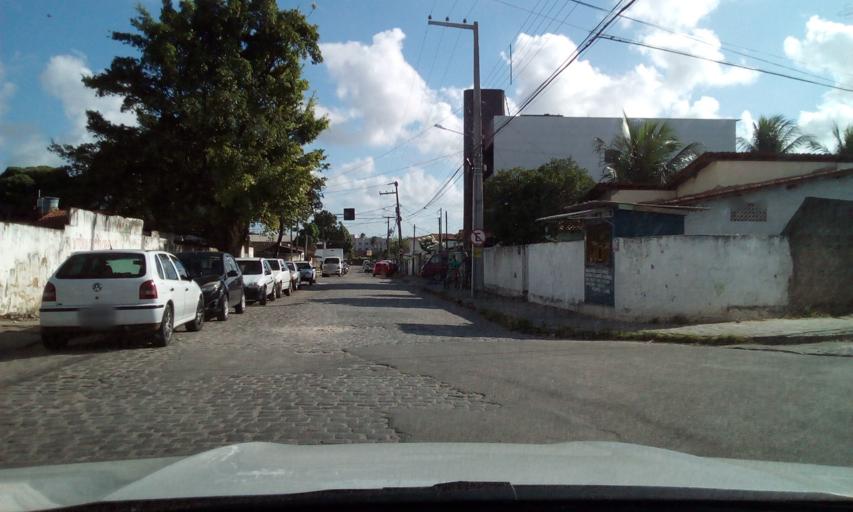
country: BR
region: Paraiba
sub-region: Bayeux
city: Bayeux
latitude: -7.1585
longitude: -34.8969
